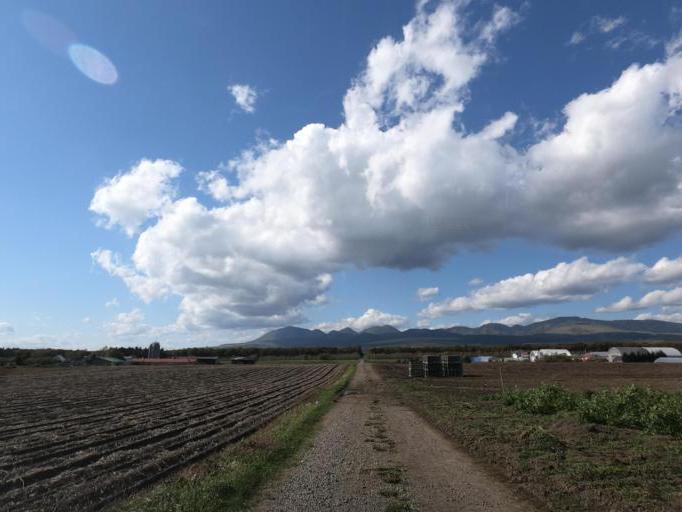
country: JP
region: Hokkaido
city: Otofuke
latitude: 43.2358
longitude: 143.2587
